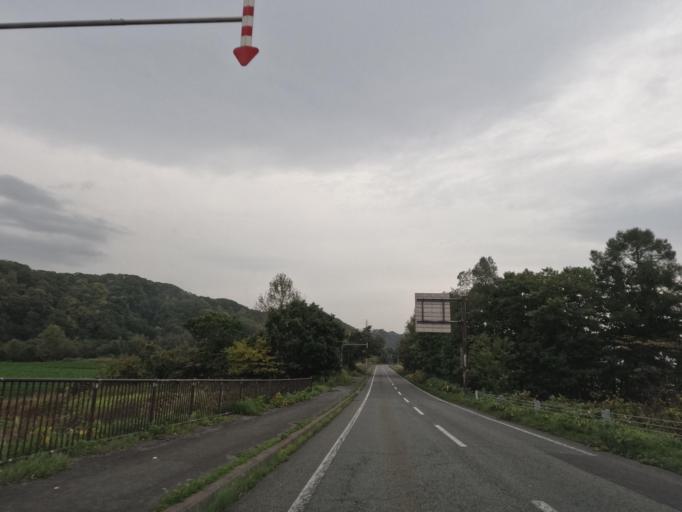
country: JP
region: Hokkaido
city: Date
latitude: 42.5179
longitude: 140.8637
